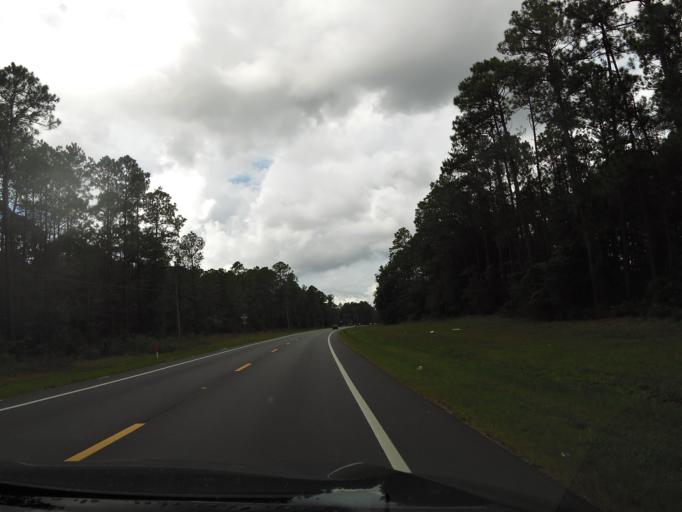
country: US
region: Florida
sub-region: Clay County
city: Middleburg
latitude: 30.0546
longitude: -81.8645
